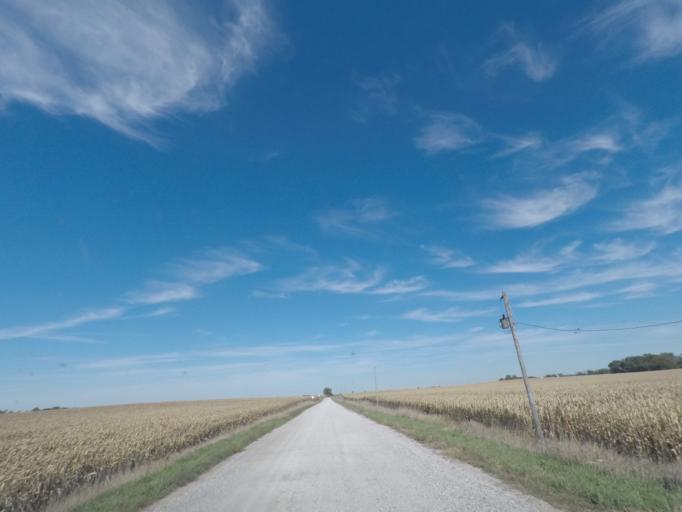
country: US
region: Iowa
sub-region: Story County
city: Nevada
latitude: 42.0193
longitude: -93.3573
